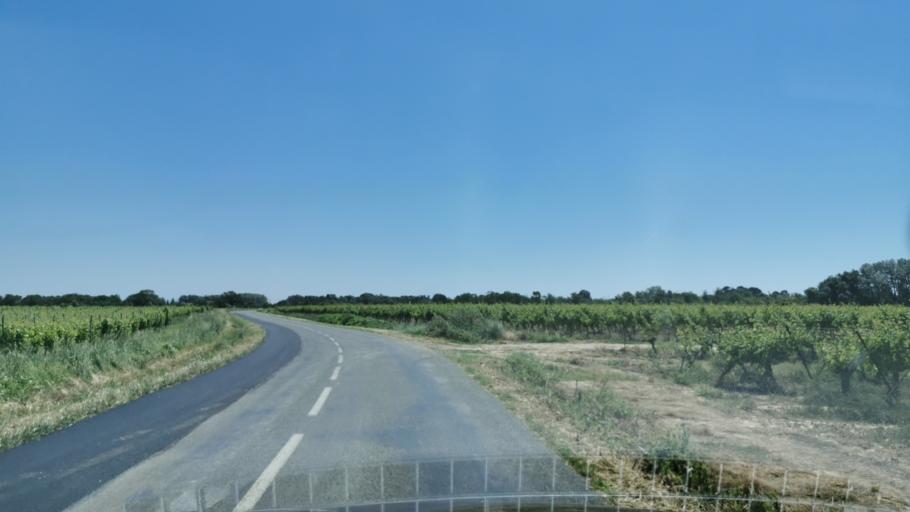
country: FR
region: Languedoc-Roussillon
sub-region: Departement de l'Aude
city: Moussan
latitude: 43.2536
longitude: 2.9624
